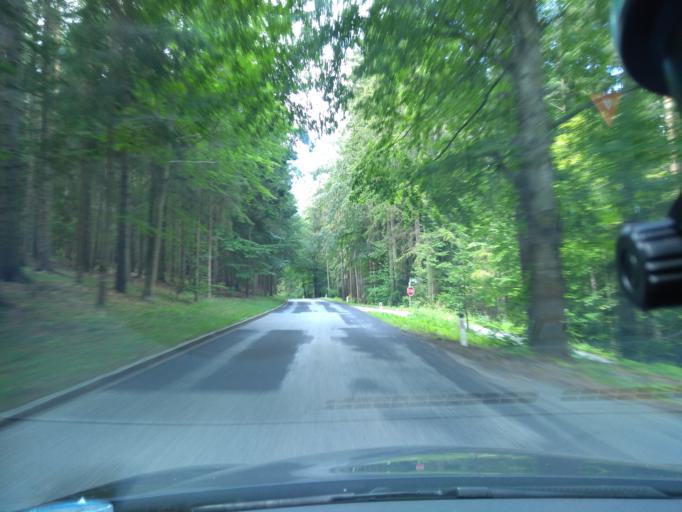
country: AT
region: Styria
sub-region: Politischer Bezirk Graz-Umgebung
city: Semriach
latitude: 47.2292
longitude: 15.4302
